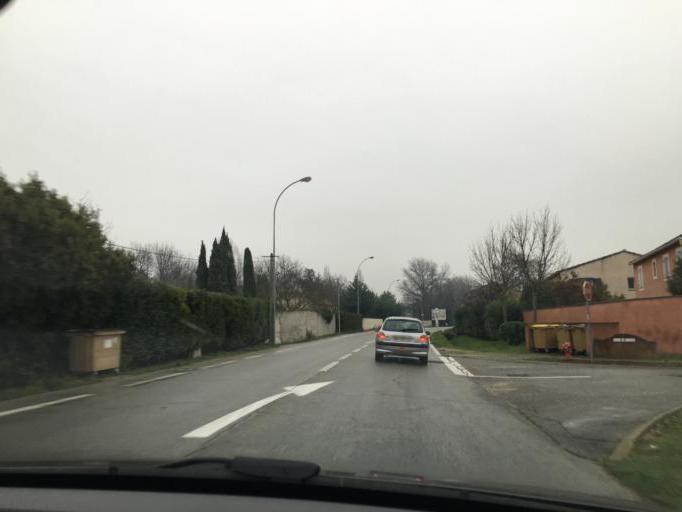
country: FR
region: Provence-Alpes-Cote d'Azur
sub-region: Departement du Vaucluse
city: L'Isle-sur-la-Sorgue
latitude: 43.9152
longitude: 5.0688
